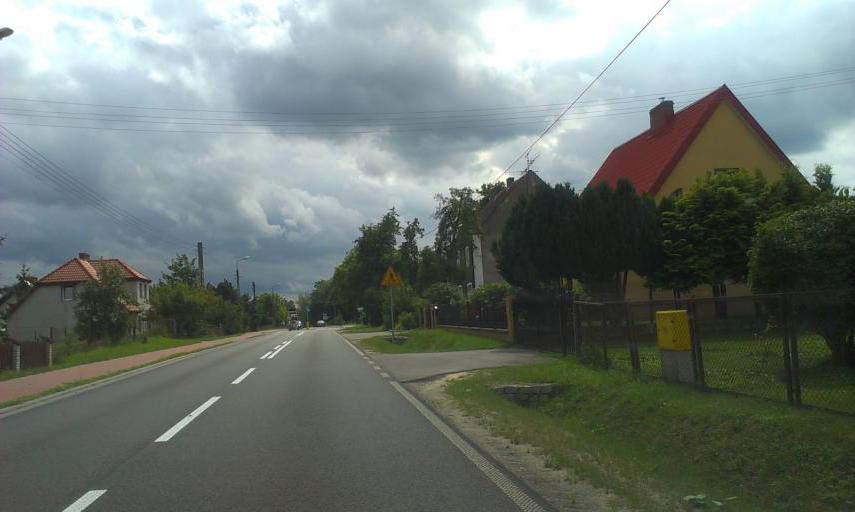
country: PL
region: West Pomeranian Voivodeship
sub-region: Koszalin
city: Koszalin
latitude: 54.0708
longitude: 16.1627
